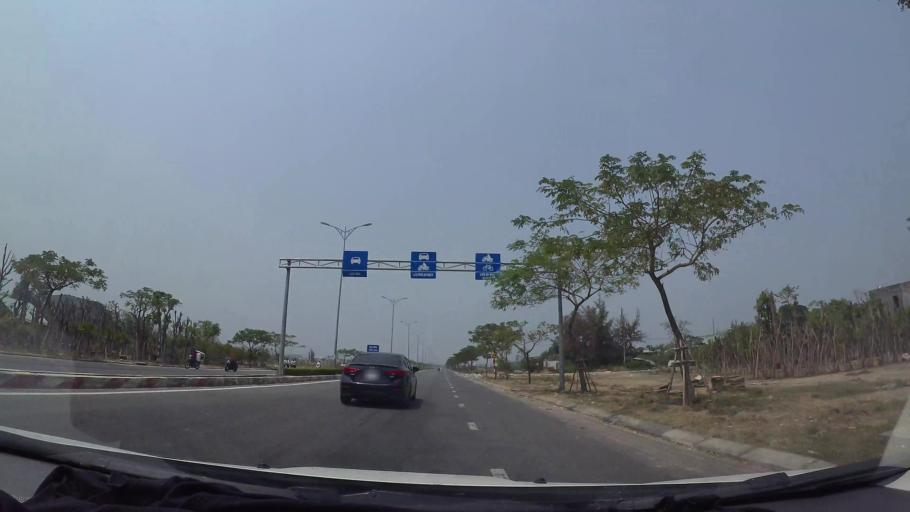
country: VN
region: Da Nang
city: Ngu Hanh Son
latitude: 15.9864
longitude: 108.2409
